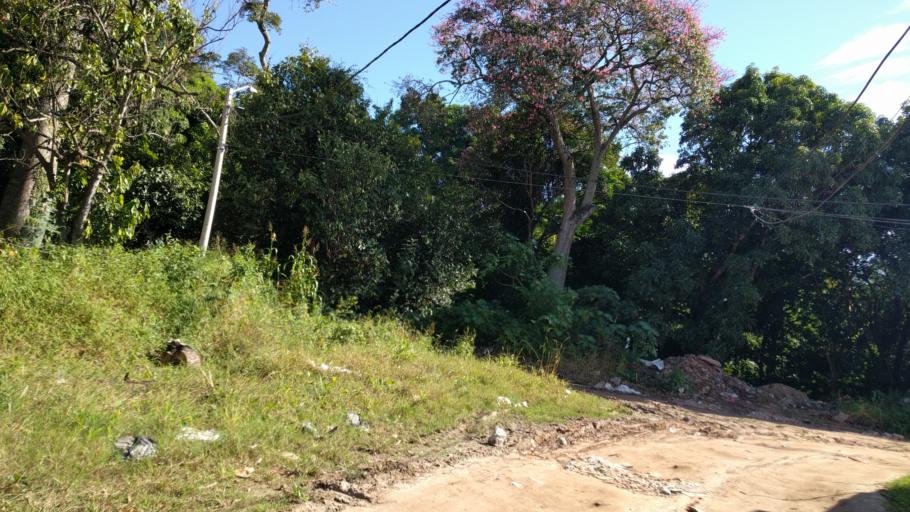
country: BO
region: Santa Cruz
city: Santa Cruz de la Sierra
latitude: -17.7981
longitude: -63.2214
